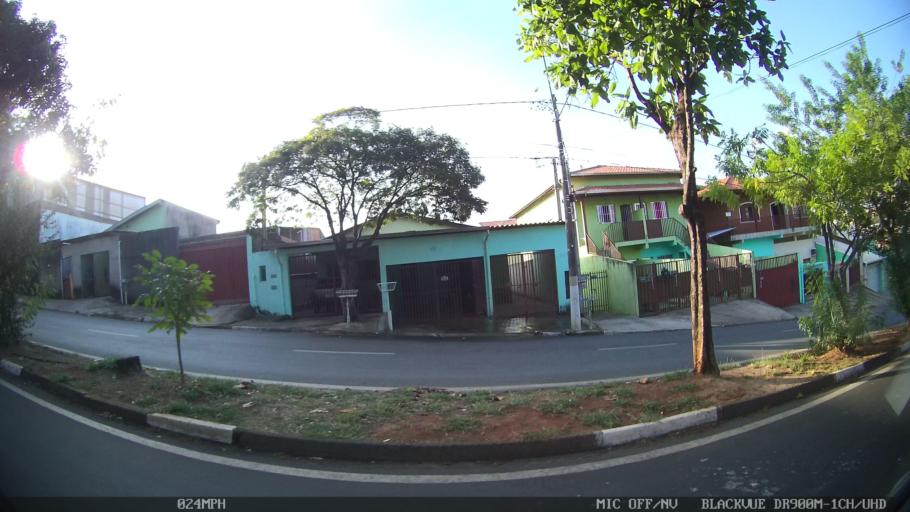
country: BR
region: Sao Paulo
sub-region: Campinas
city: Campinas
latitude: -22.9711
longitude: -47.1205
